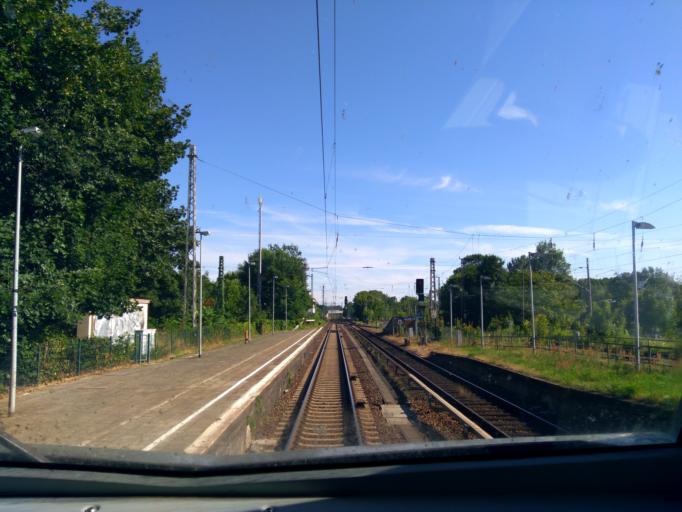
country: DE
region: Brandenburg
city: Konigs Wusterhausen
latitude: 52.2972
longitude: 13.6314
